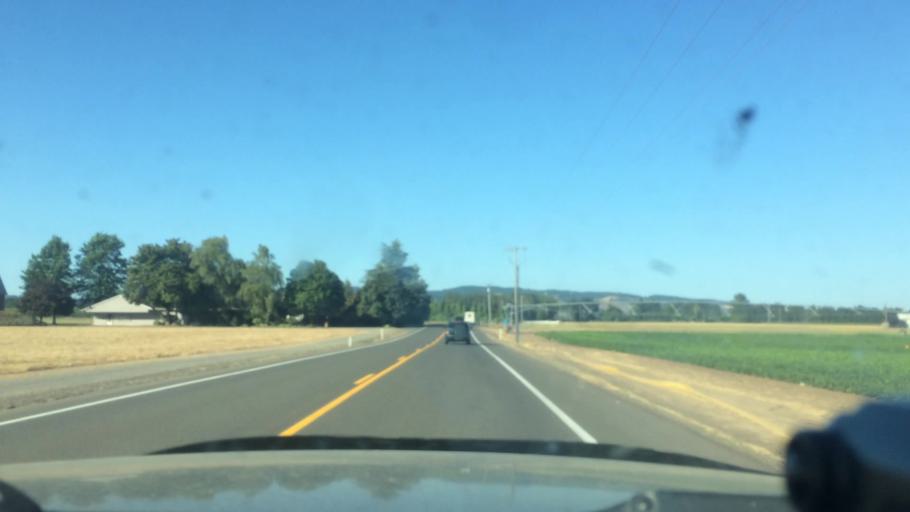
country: US
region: Oregon
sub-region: Yamhill County
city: Newberg
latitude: 45.2387
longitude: -122.9566
